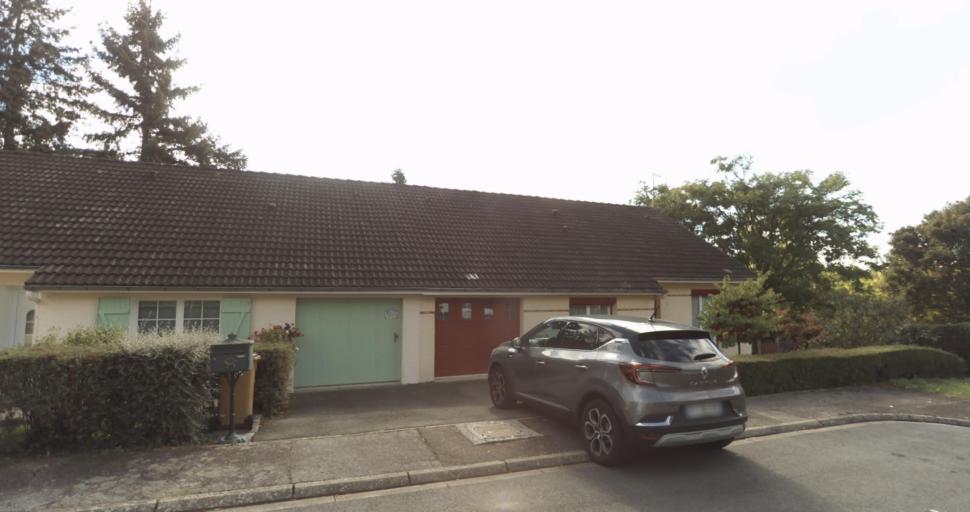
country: FR
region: Centre
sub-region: Departement d'Eure-et-Loir
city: Garnay
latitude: 48.7224
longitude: 1.3237
